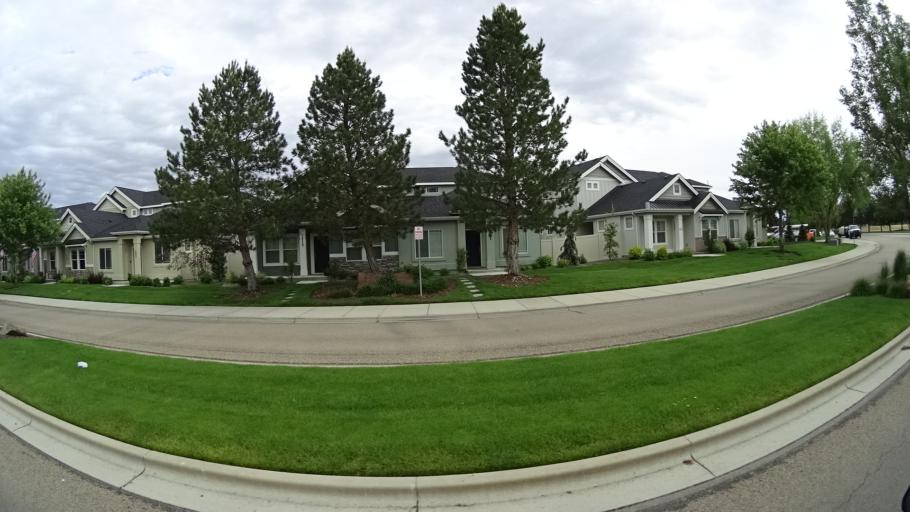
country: US
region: Idaho
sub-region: Ada County
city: Star
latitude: 43.6910
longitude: -116.5045
